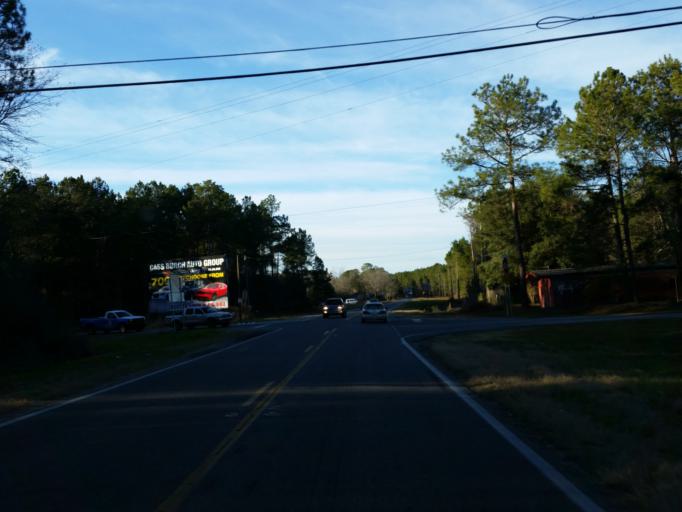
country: US
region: Georgia
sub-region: Cook County
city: Sparks
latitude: 31.2136
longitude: -83.4539
